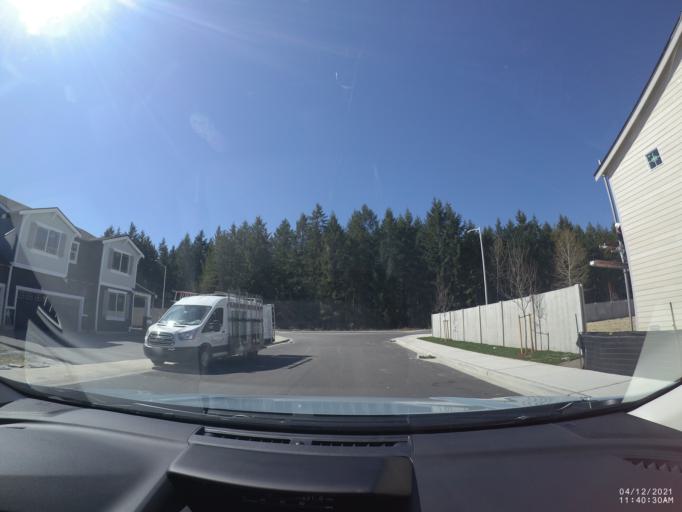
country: US
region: Washington
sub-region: Pierce County
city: South Hill
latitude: 47.0925
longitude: -122.2574
